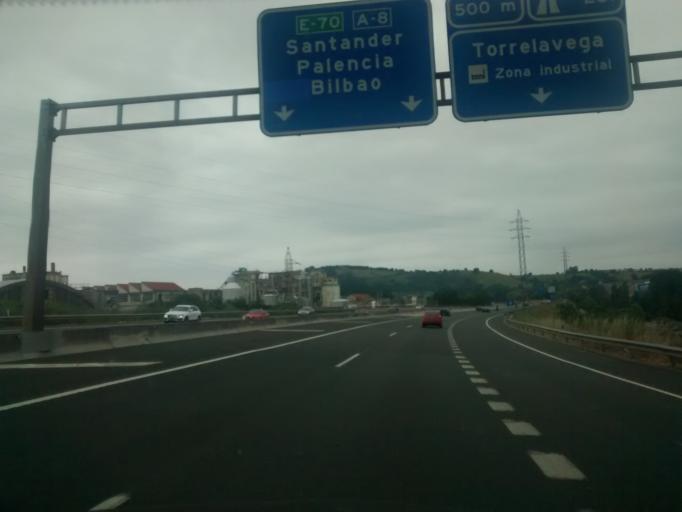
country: ES
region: Cantabria
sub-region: Provincia de Cantabria
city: Torrelavega
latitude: 43.3566
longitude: -4.0606
